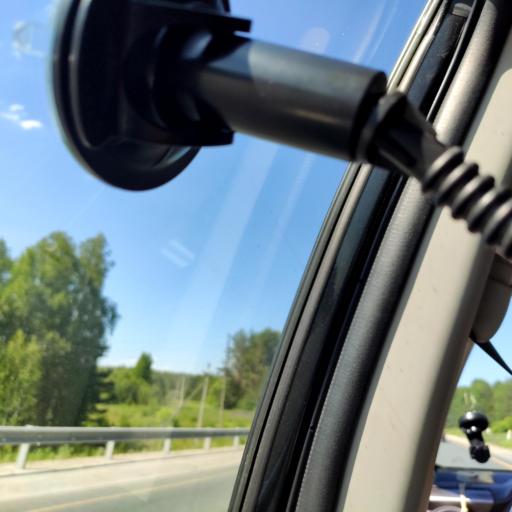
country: RU
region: Mariy-El
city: Pomary
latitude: 55.9972
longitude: 48.3825
